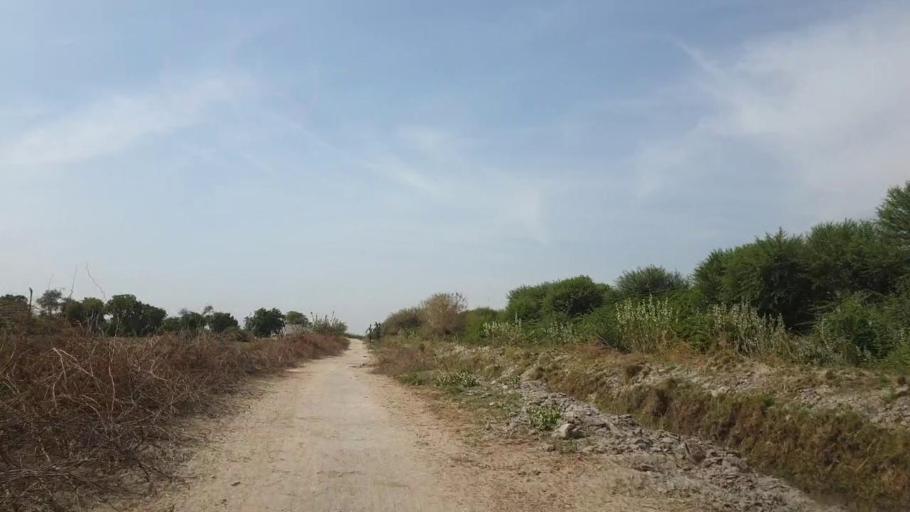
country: PK
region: Sindh
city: Kunri
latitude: 25.1946
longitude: 69.5659
